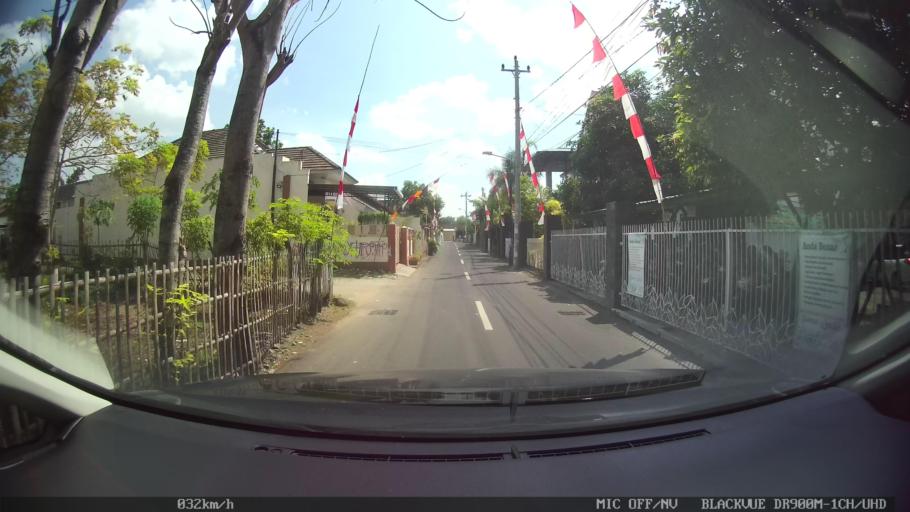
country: ID
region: Daerah Istimewa Yogyakarta
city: Yogyakarta
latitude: -7.8269
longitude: 110.3880
